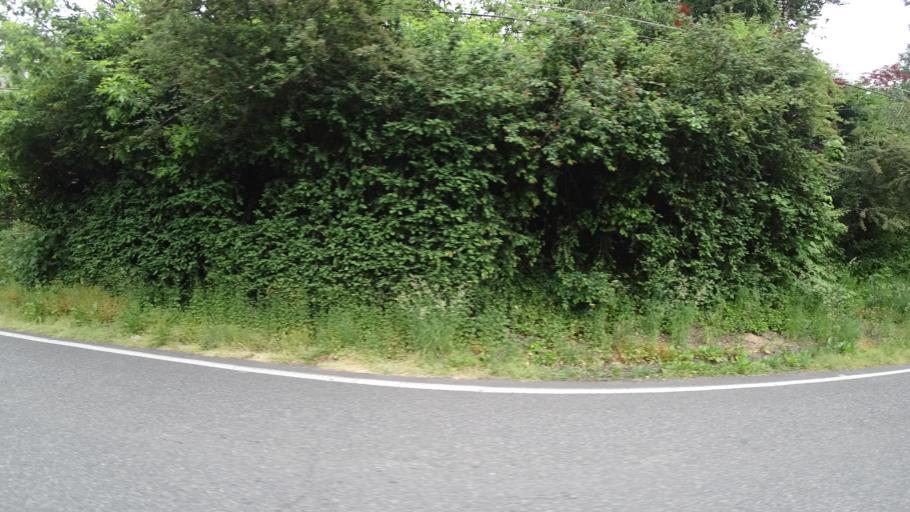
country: US
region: Oregon
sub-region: Multnomah County
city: Portland
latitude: 45.5059
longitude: -122.6978
